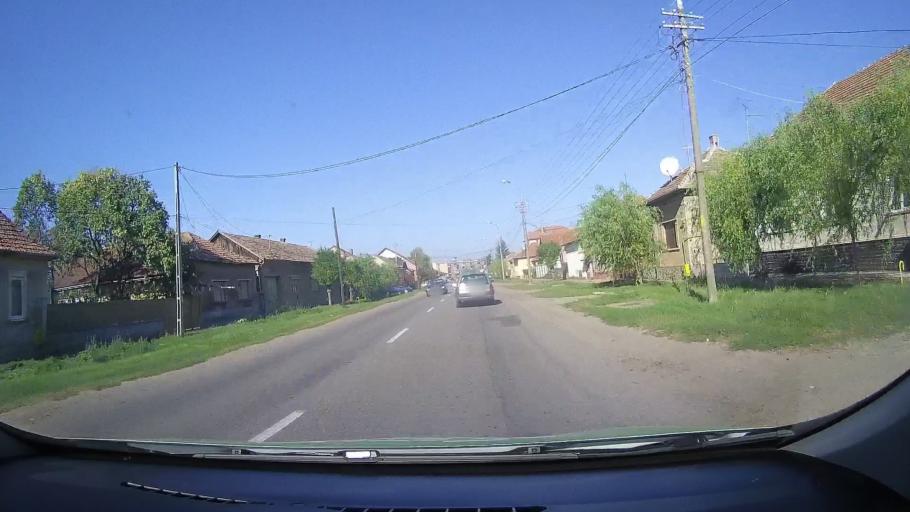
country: RO
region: Satu Mare
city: Carei
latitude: 47.6784
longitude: 22.4743
